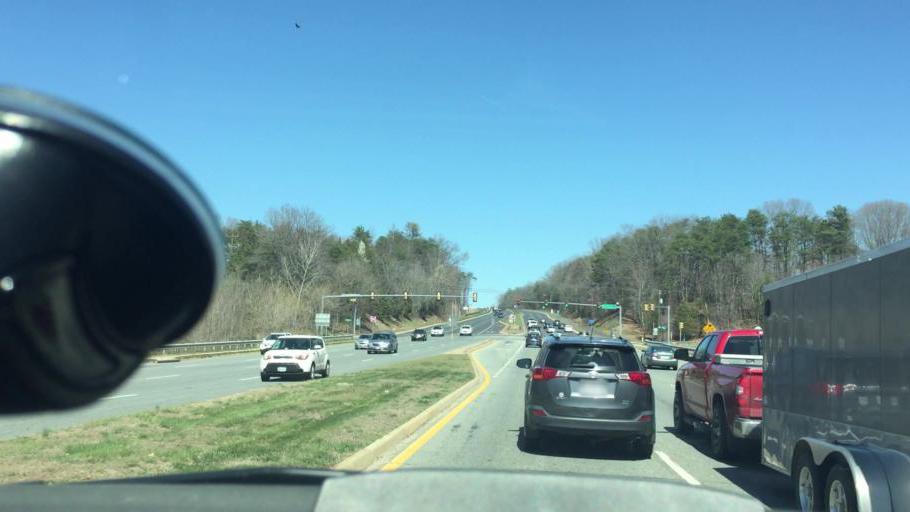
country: US
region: Virginia
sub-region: Albemarle County
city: Hollymead
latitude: 38.1015
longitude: -78.4609
